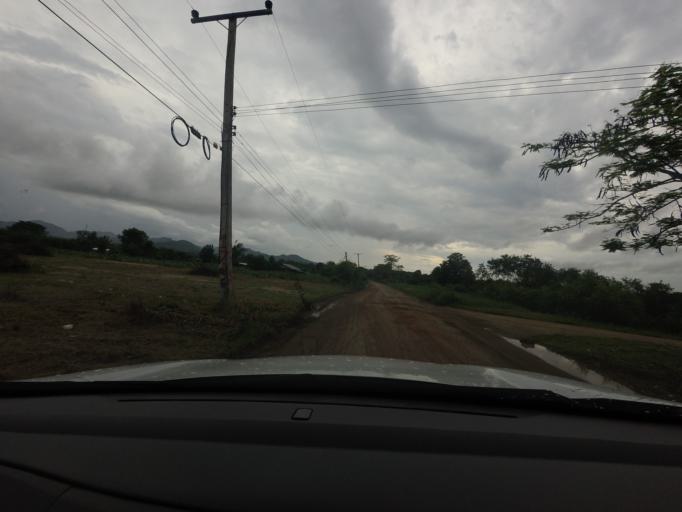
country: TH
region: Nakhon Ratchasima
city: Pak Chong
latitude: 14.6488
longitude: 101.4305
